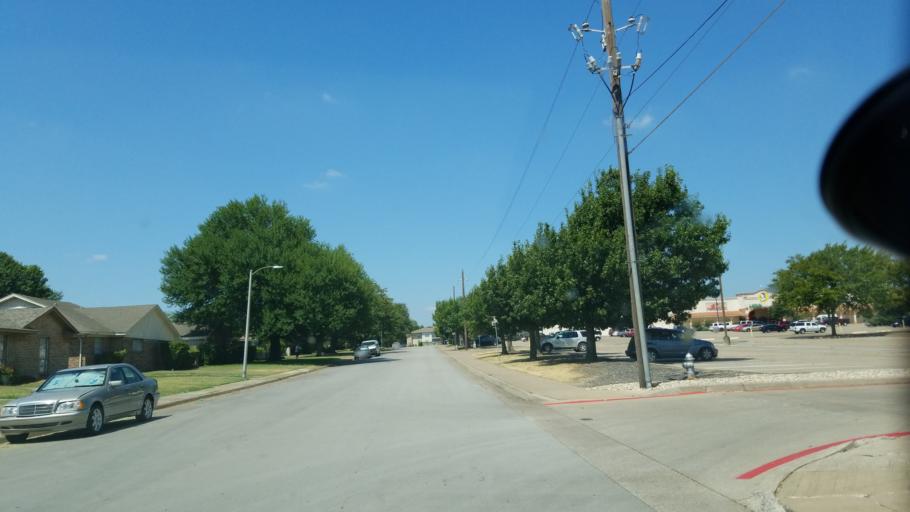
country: US
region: Texas
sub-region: Dallas County
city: Duncanville
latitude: 32.6576
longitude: -96.8922
